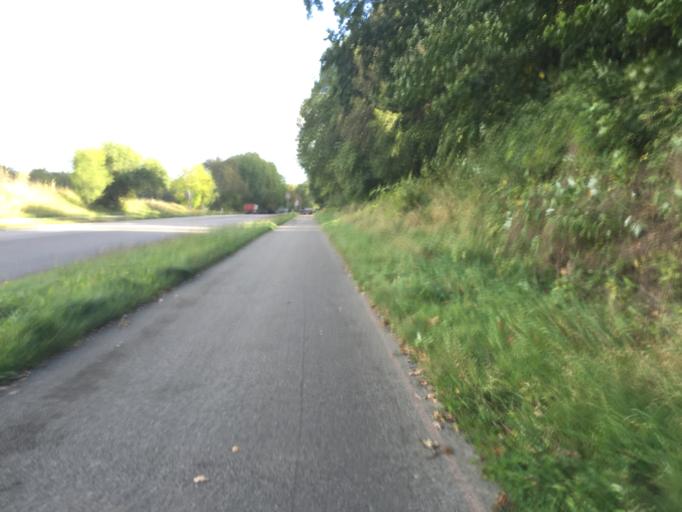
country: DK
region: Capital Region
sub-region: Fureso Kommune
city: Stavnsholt
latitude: 55.7732
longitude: 12.4204
